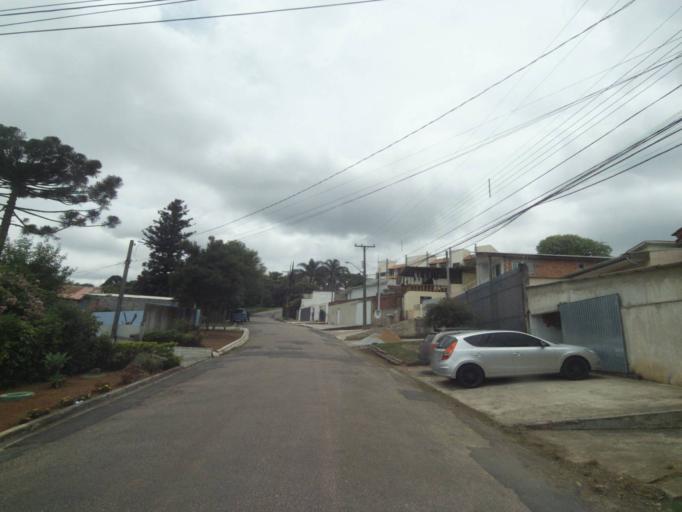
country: BR
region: Parana
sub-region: Curitiba
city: Curitiba
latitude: -25.3916
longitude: -49.2914
